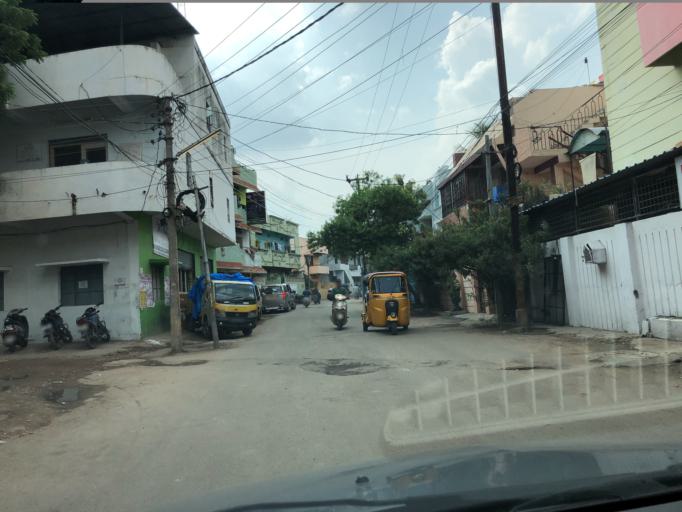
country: IN
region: Telangana
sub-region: Hyderabad
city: Malkajgiri
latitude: 17.4463
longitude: 78.4806
